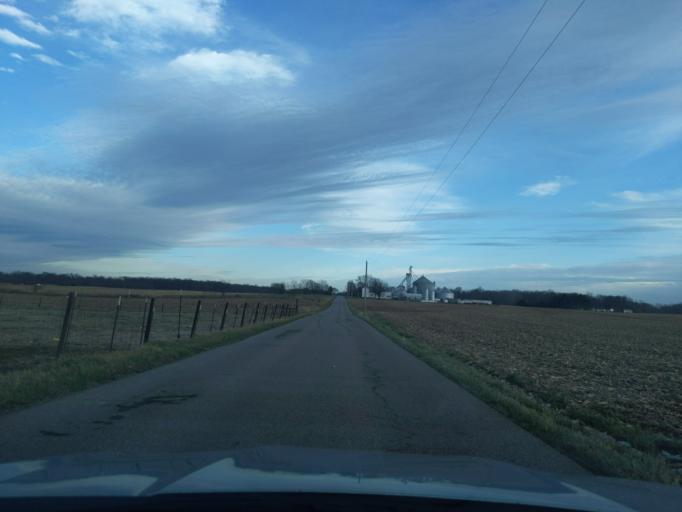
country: US
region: Indiana
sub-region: Decatur County
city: Westport
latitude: 39.2345
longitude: -85.5530
